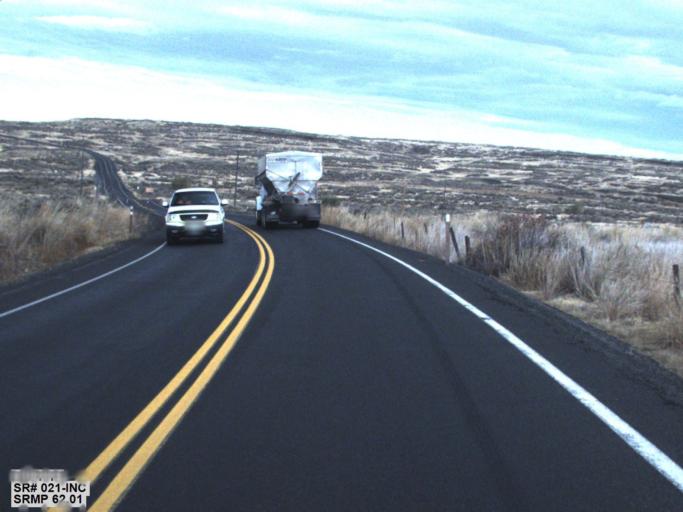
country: US
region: Washington
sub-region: Adams County
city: Ritzville
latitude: 47.4153
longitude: -118.6836
